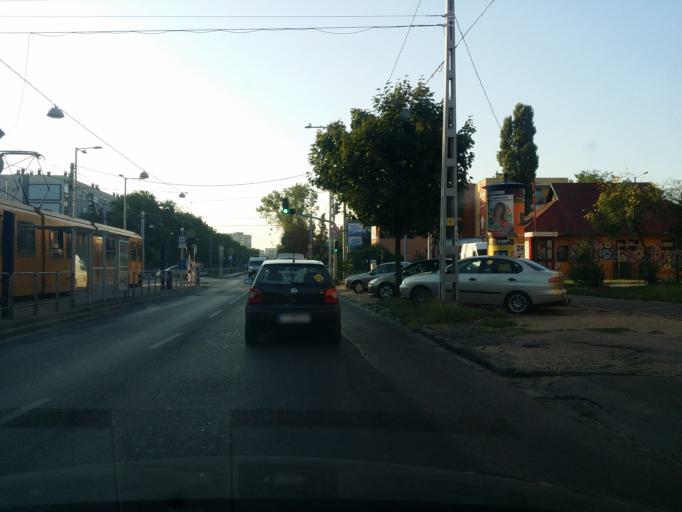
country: HU
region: Budapest
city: Budapest XIV. keruelet
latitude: 47.5097
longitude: 19.1285
